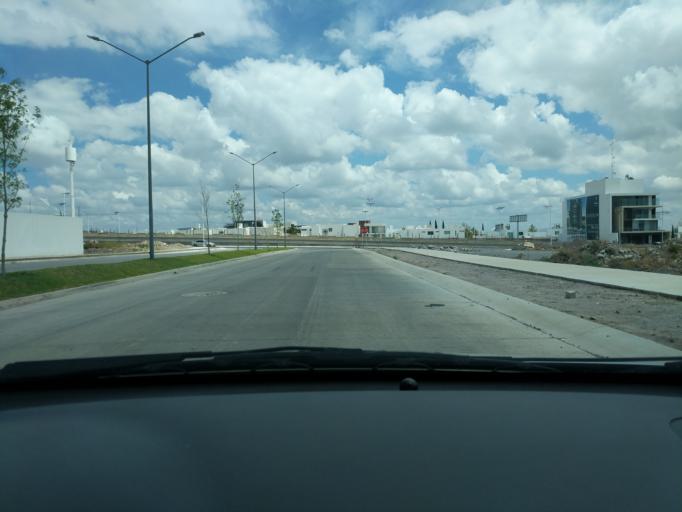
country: MX
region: San Luis Potosi
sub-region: Mexquitic de Carmona
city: Guadalupe Victoria
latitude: 22.1668
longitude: -101.0460
